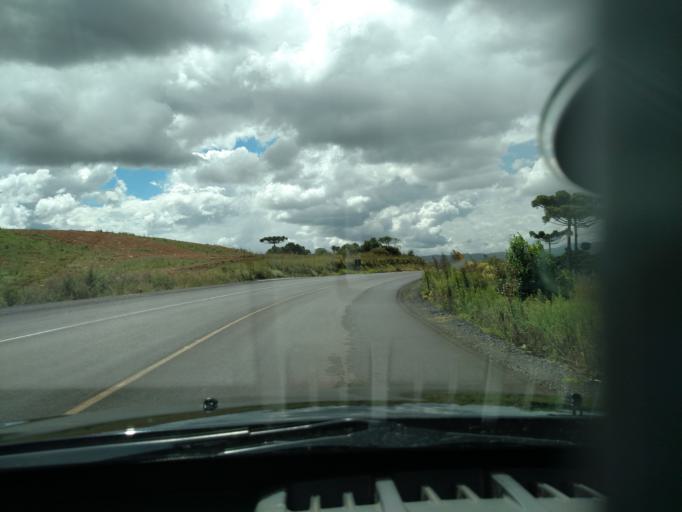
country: BR
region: Santa Catarina
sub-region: Sao Joaquim
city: Sao Joaquim
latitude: -28.1104
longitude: -50.0510
